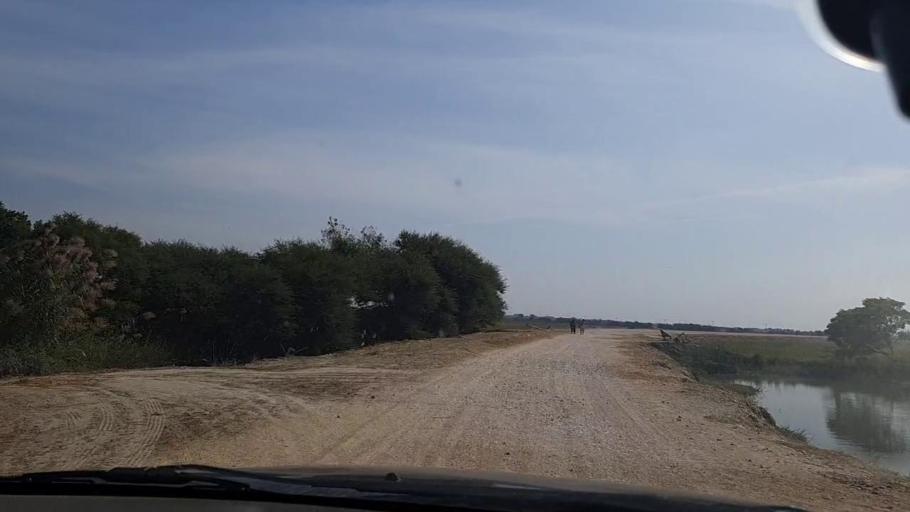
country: PK
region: Sindh
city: Mirpur Batoro
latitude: 24.7322
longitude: 68.2756
